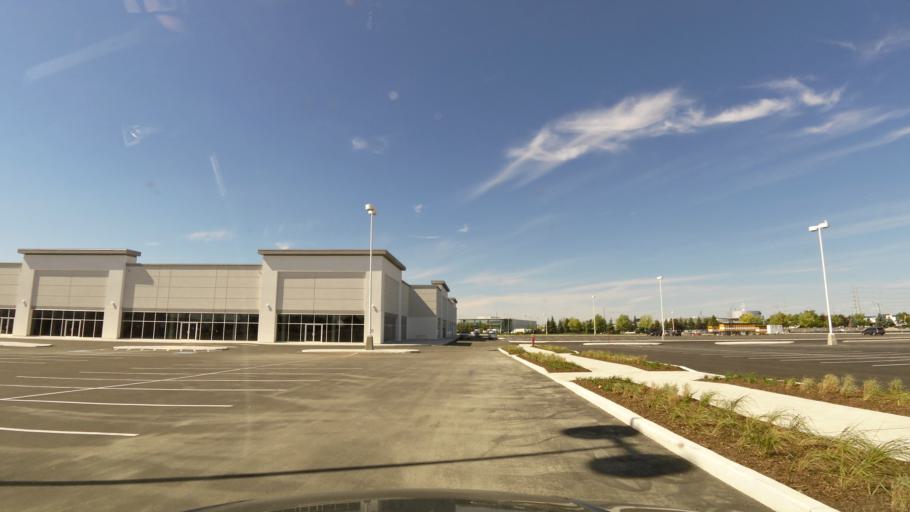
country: CA
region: Ontario
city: Mississauga
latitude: 43.6117
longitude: -79.6985
